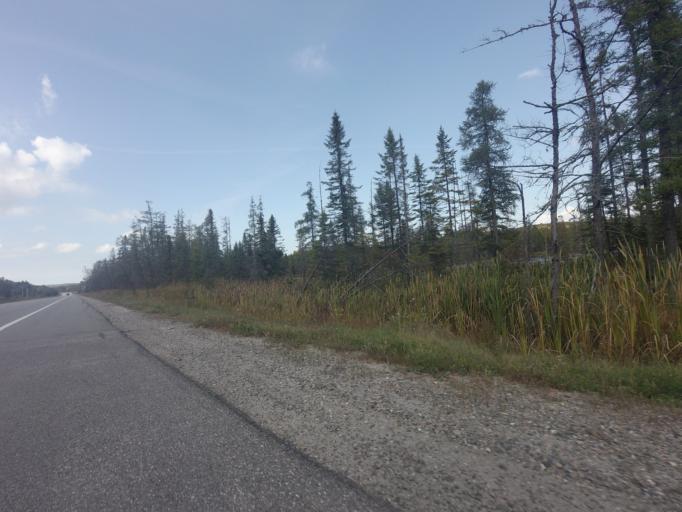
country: CA
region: Quebec
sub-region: Laurentides
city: Mont-Laurier
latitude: 46.5580
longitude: -75.6182
